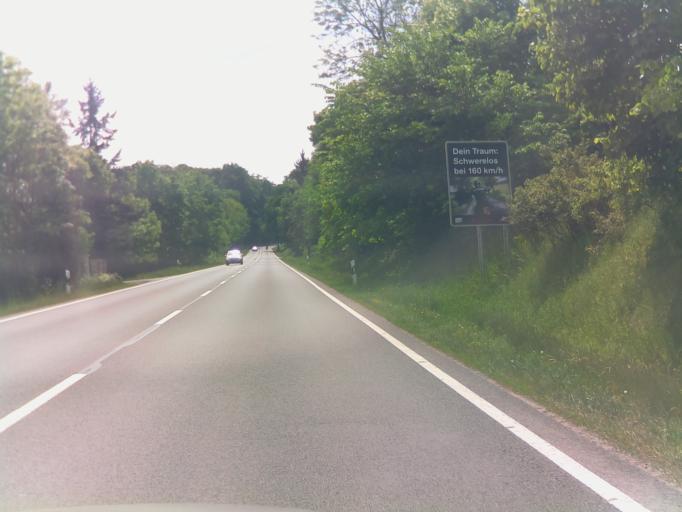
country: DE
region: Saxony-Anhalt
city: Blankenburg
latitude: 51.7589
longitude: 10.9574
